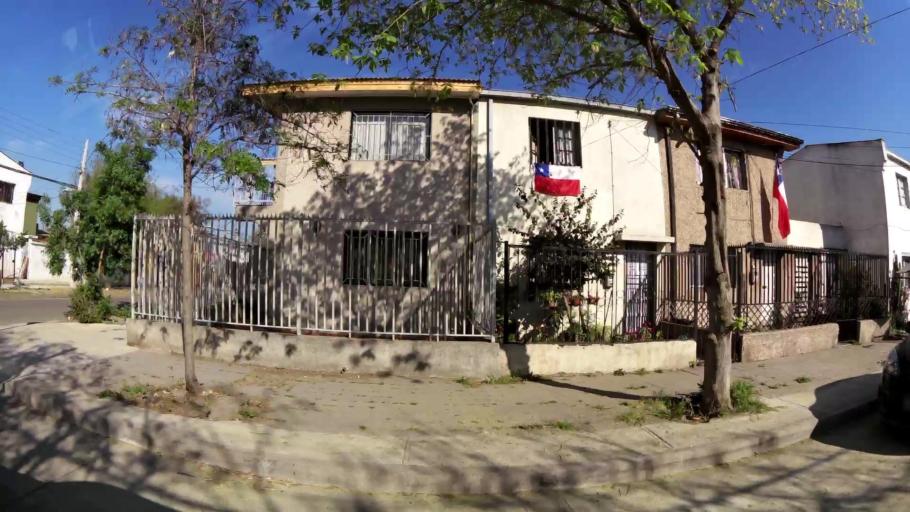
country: CL
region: Santiago Metropolitan
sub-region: Provincia de Santiago
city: Santiago
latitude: -33.4107
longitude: -70.6651
